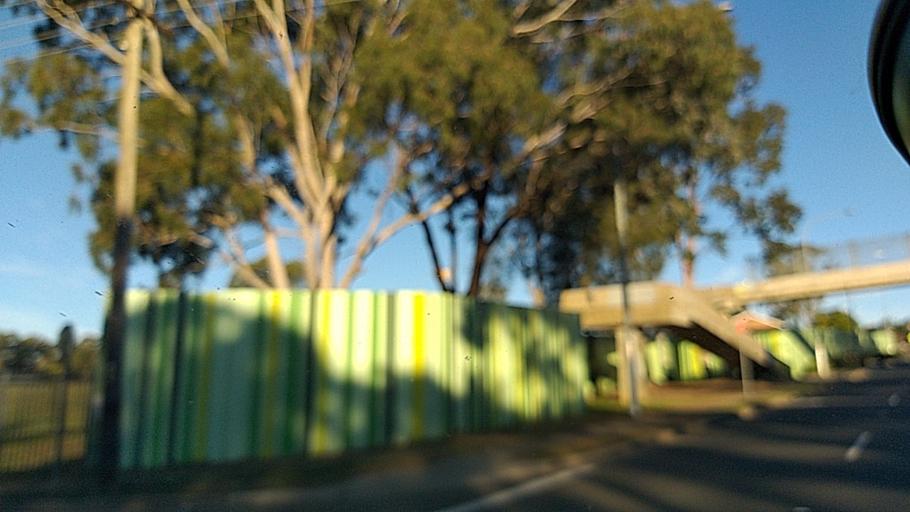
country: AU
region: New South Wales
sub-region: Campbelltown Municipality
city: Campbelltown
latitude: -34.0605
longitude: 150.8251
